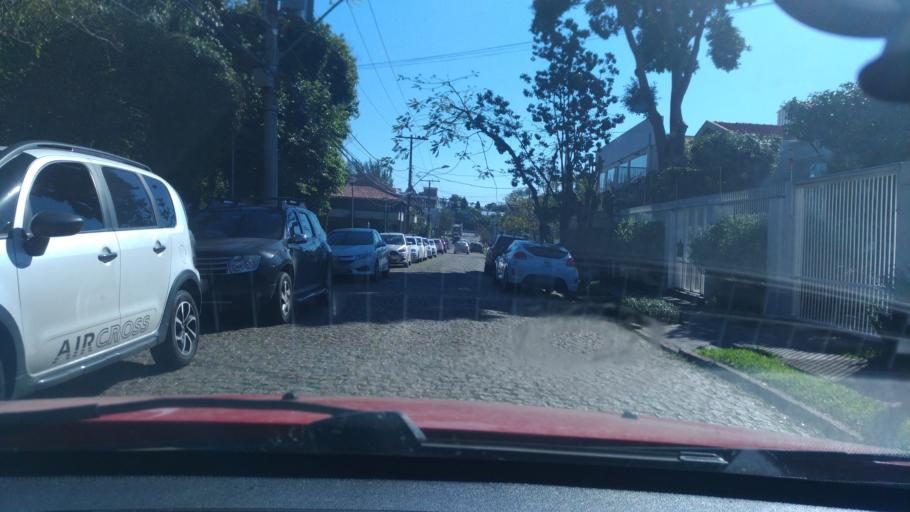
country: BR
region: Rio Grande do Sul
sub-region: Porto Alegre
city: Porto Alegre
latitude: -30.0302
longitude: -51.1687
